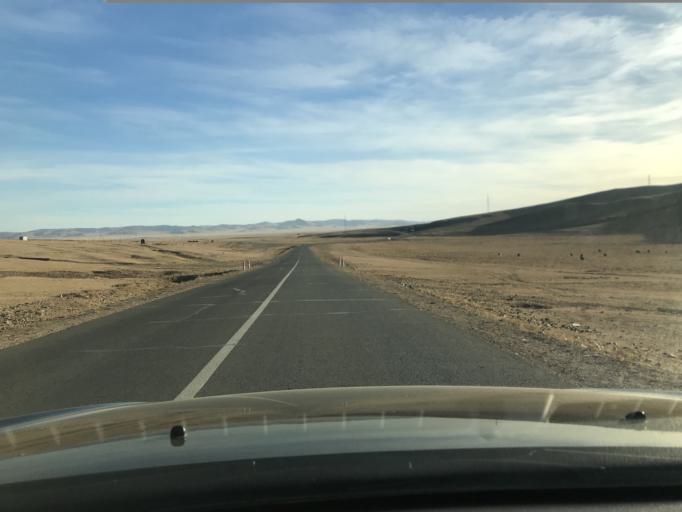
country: MN
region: Central Aimak
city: Dzuunmod
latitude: 47.8012
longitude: 107.3237
